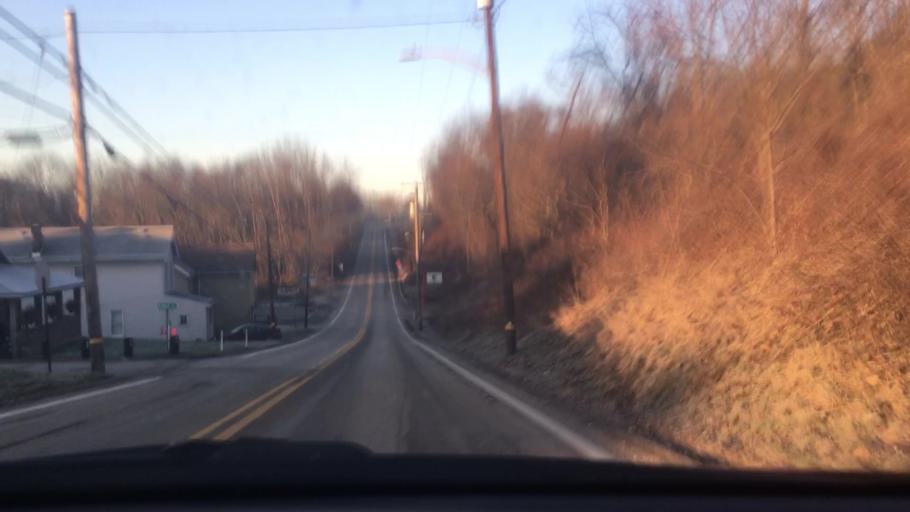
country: US
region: Pennsylvania
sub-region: Allegheny County
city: Jefferson Hills
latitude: 40.2526
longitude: -79.9273
